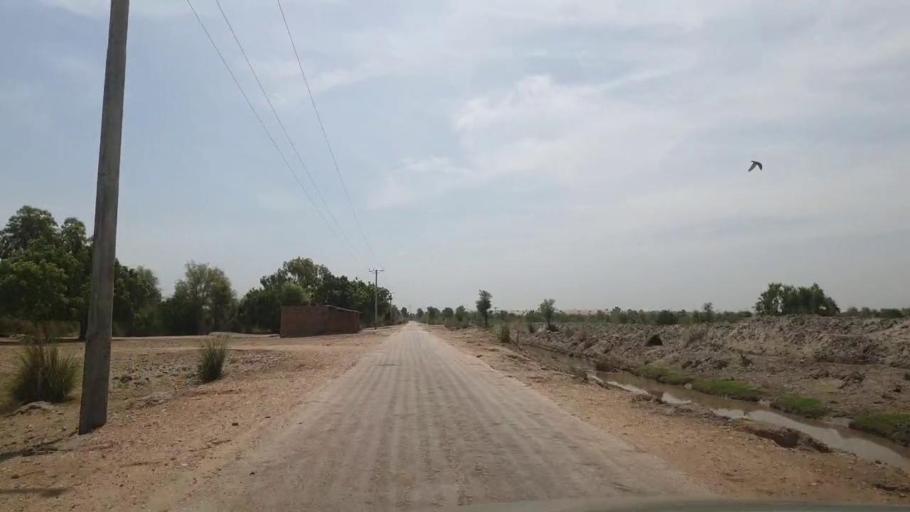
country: PK
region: Sindh
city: Kot Diji
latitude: 27.1132
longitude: 69.0163
